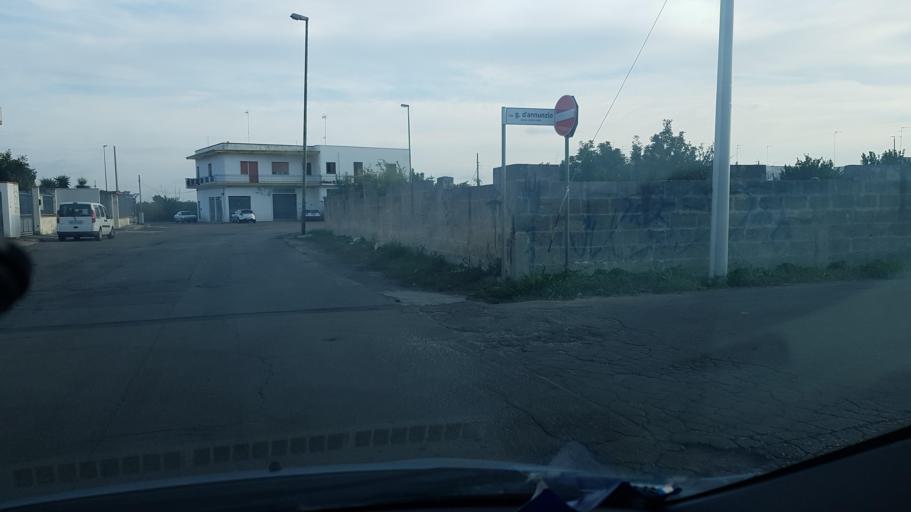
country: IT
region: Apulia
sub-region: Provincia di Lecce
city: Veglie
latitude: 40.3332
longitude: 17.9745
